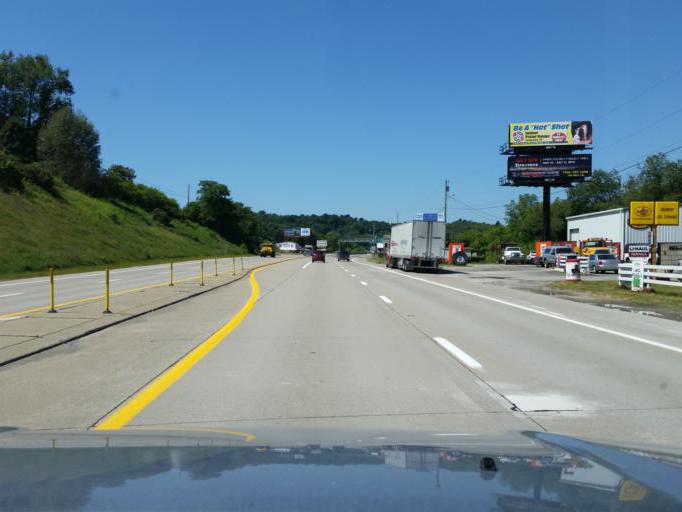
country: US
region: Pennsylvania
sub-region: Westmoreland County
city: Delmont
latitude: 40.3992
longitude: -79.5609
